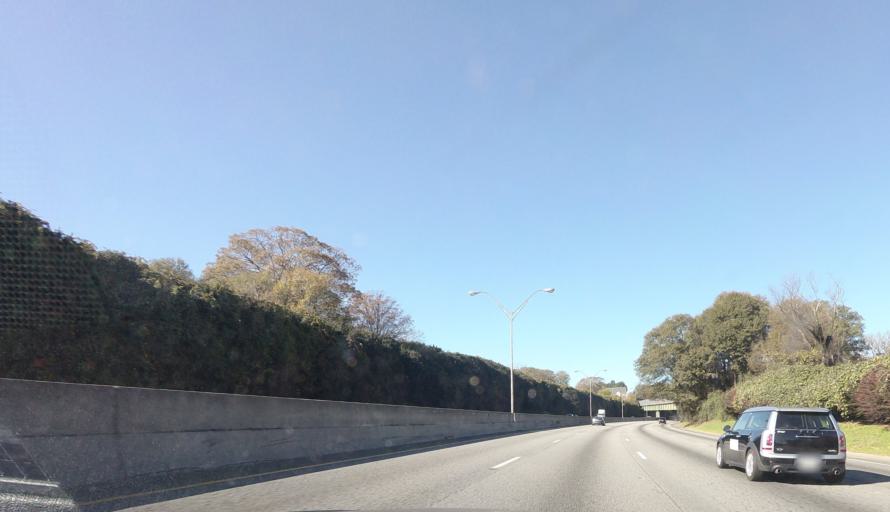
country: US
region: Georgia
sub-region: Fulton County
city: Atlanta
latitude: 33.7470
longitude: -84.4361
